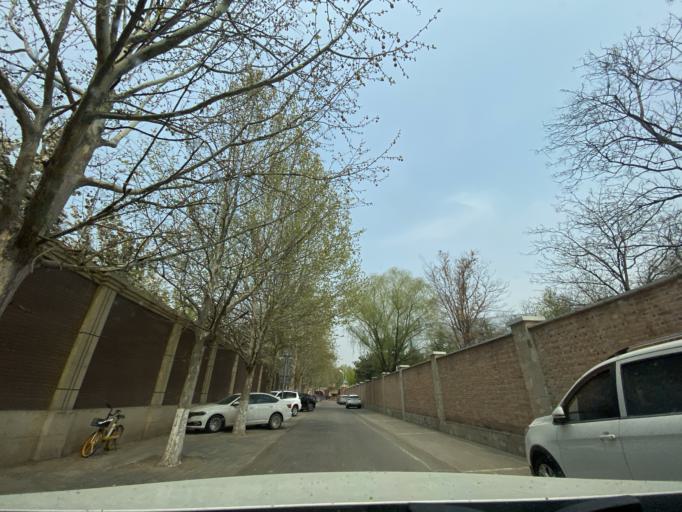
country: CN
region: Beijing
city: Sijiqing
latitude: 39.9419
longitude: 116.2458
